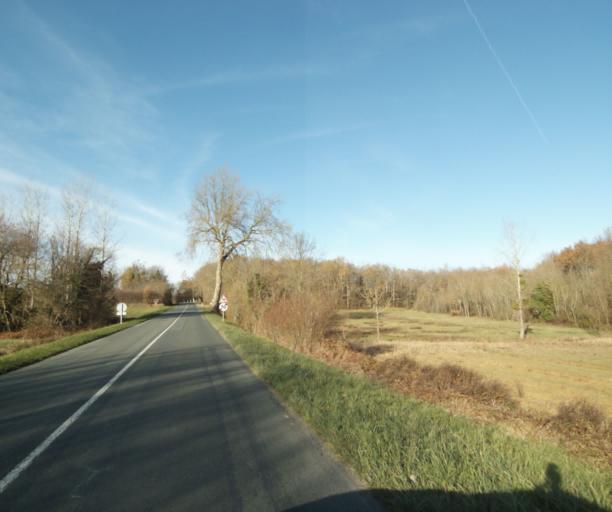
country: FR
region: Poitou-Charentes
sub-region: Departement de la Charente-Maritime
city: Burie
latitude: 45.7913
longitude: -0.4373
